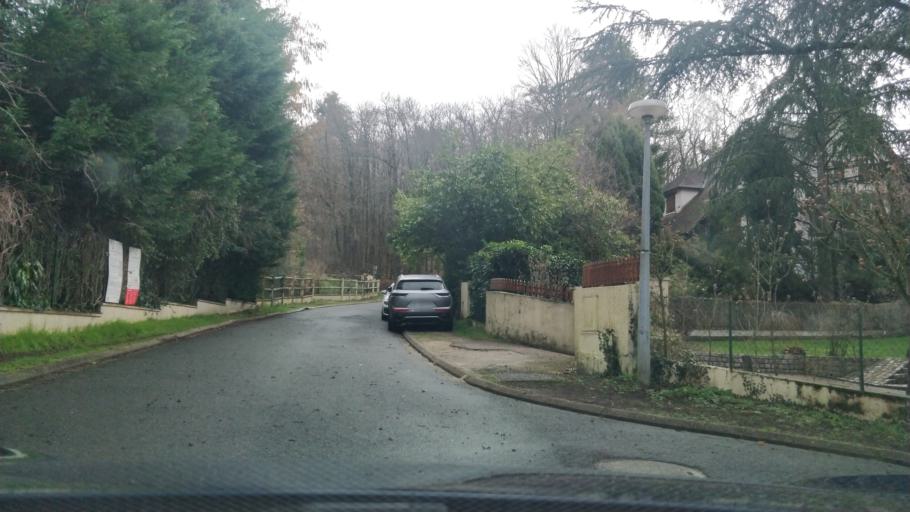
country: FR
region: Ile-de-France
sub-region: Departement de l'Essonne
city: Briis-sous-Forges
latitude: 48.6323
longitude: 2.1220
